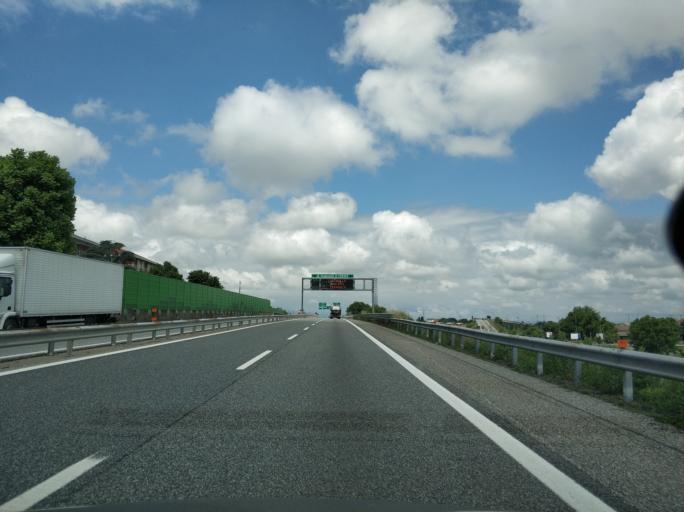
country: IT
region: Piedmont
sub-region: Provincia di Torino
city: Settimo Torinese
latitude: 45.1236
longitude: 7.7326
